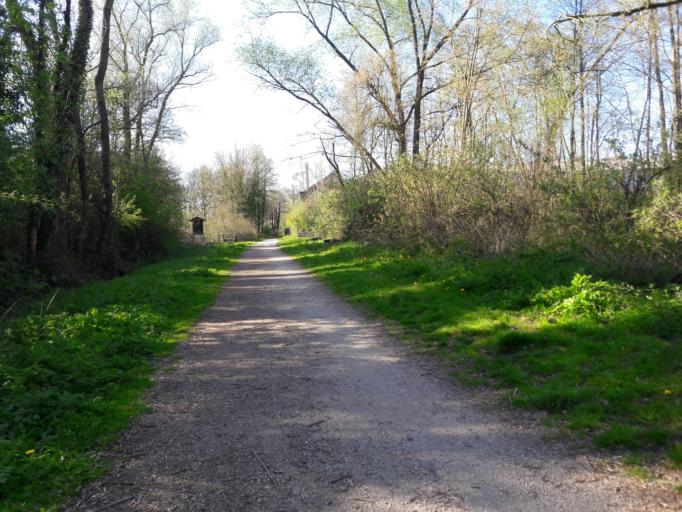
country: FR
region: Nord-Pas-de-Calais
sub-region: Departement du Nord
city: Ferriere-la-Grande
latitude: 50.2503
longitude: 4.0064
